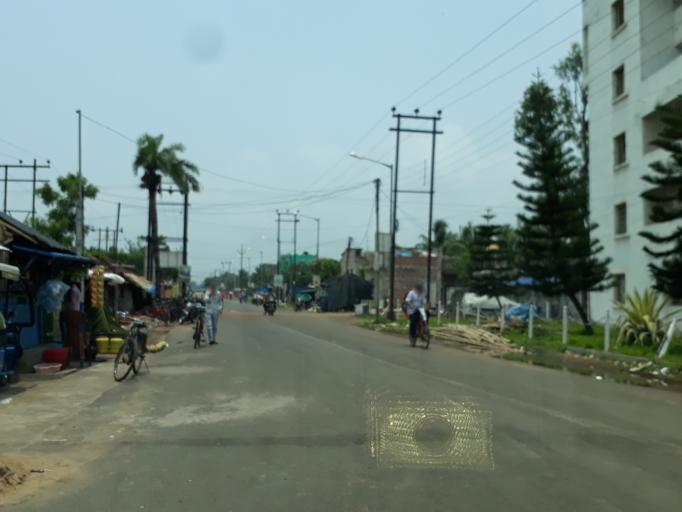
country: IN
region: West Bengal
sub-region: Purba Medinipur
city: Haldia
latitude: 22.0494
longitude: 88.0677
